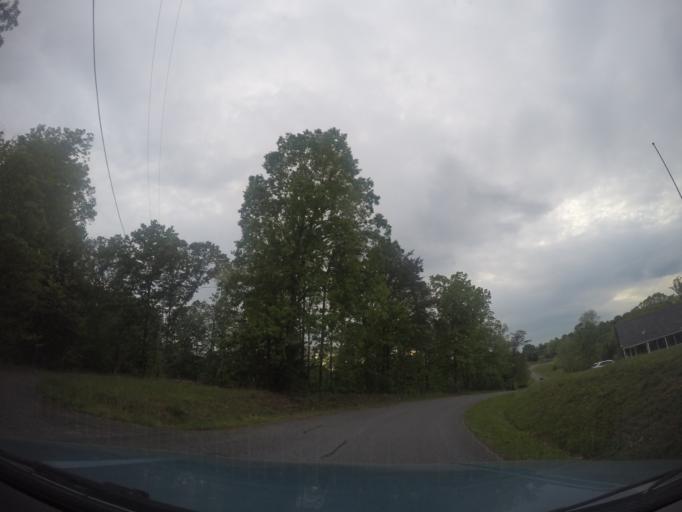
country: US
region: Virginia
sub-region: City of Lynchburg
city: Lynchburg
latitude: 37.3843
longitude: -79.1027
